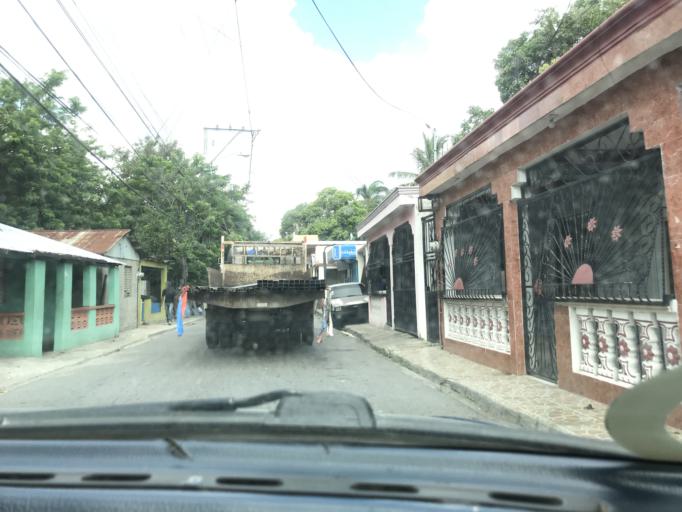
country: DO
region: Santiago
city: Santiago de los Caballeros
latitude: 19.4528
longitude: -70.7283
